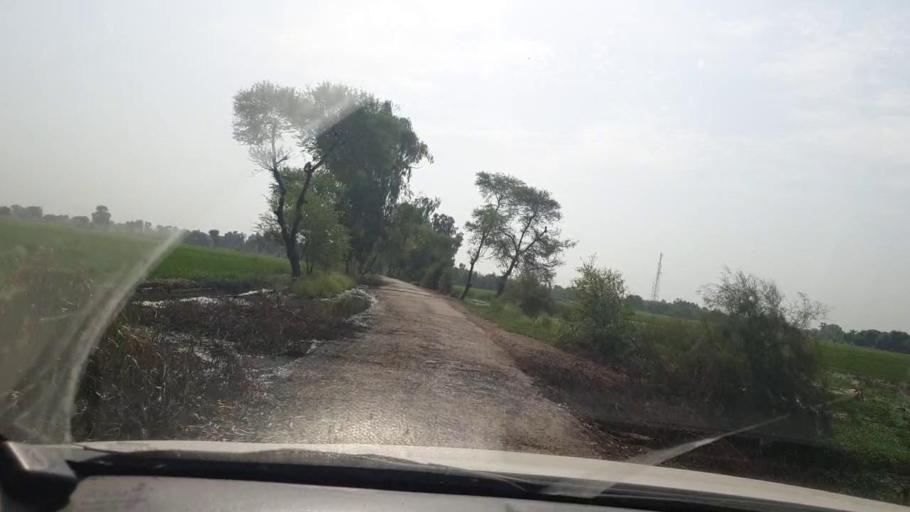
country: PK
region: Sindh
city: Chak
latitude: 27.8308
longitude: 68.7698
